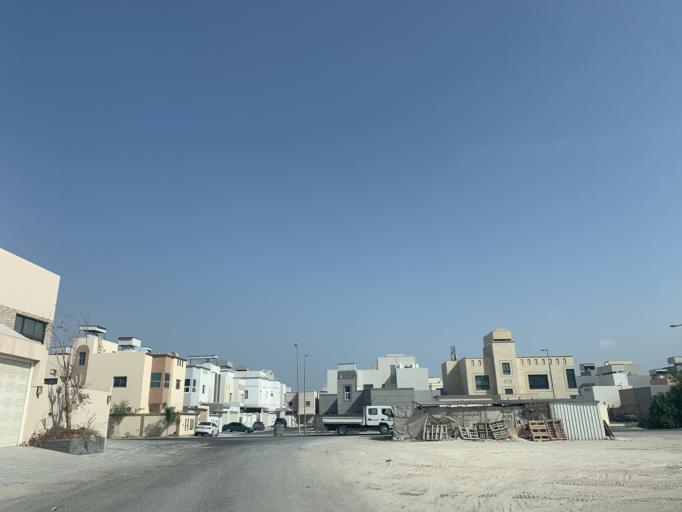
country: BH
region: Central Governorate
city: Madinat Hamad
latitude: 26.1352
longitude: 50.4909
